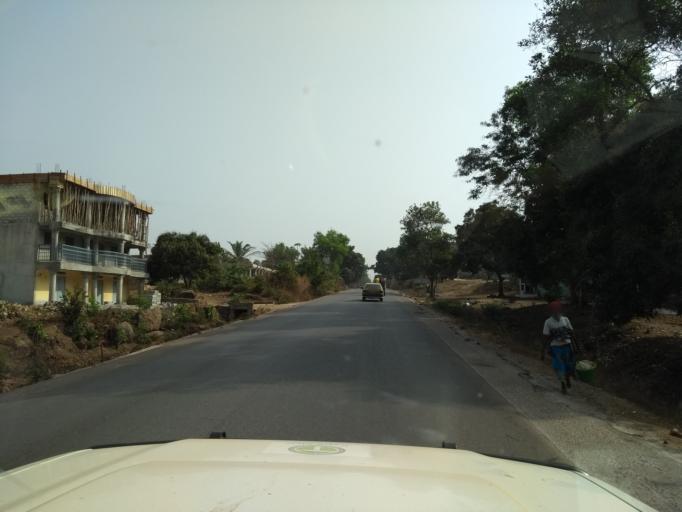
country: GN
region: Kindia
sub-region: Prefecture de Dubreka
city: Dubreka
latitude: 9.8473
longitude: -13.4858
